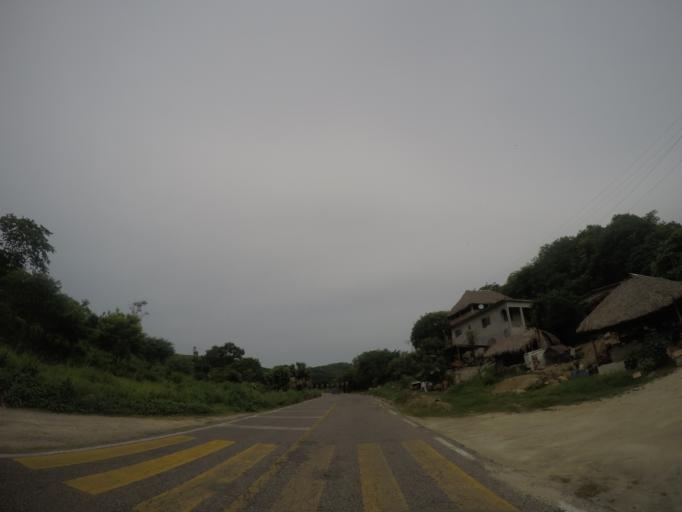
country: MX
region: Oaxaca
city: San Pedro Mixtepec
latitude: 15.9568
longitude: -97.2171
